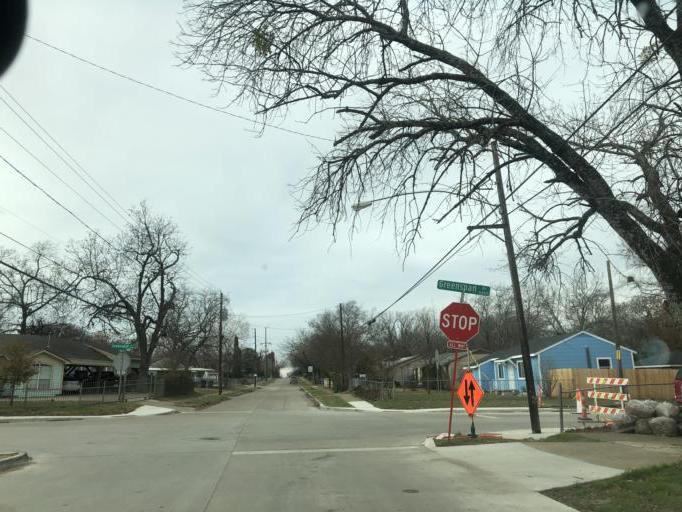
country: US
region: Texas
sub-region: Dallas County
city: Duncanville
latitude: 32.6693
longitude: -96.8289
